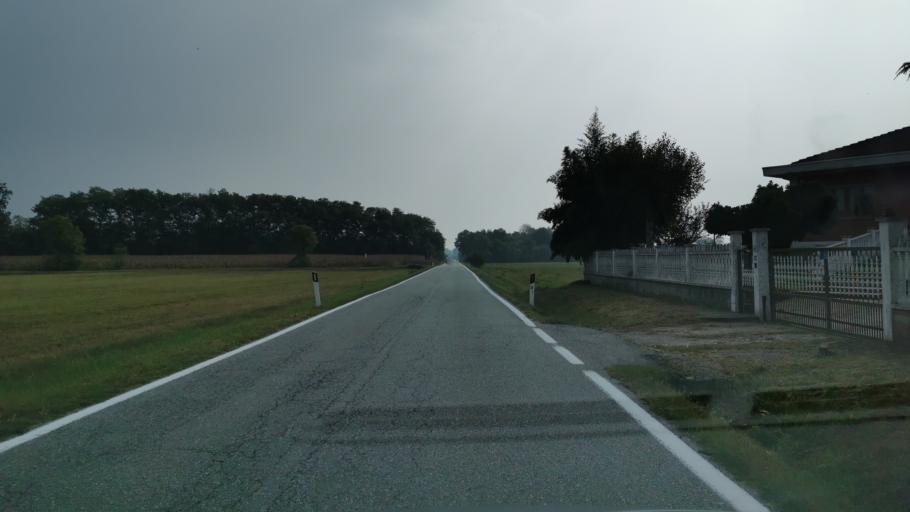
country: IT
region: Piedmont
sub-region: Provincia di Torino
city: San Benigno Canavese
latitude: 45.2227
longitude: 7.7690
